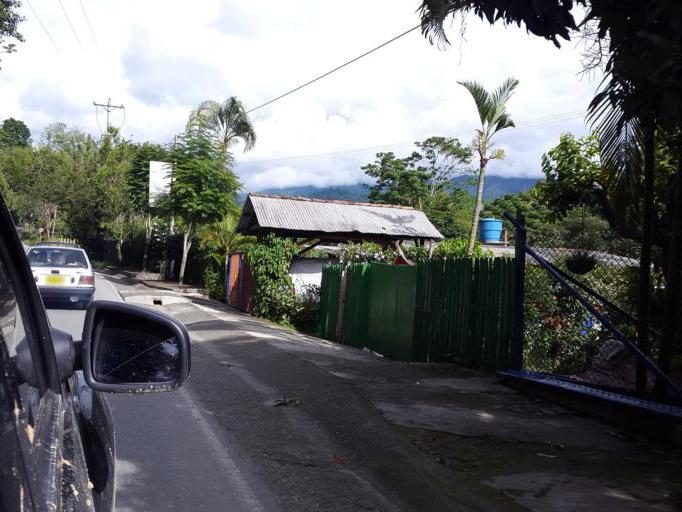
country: CO
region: Quindio
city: Cordoba
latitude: 4.4055
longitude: -75.7313
